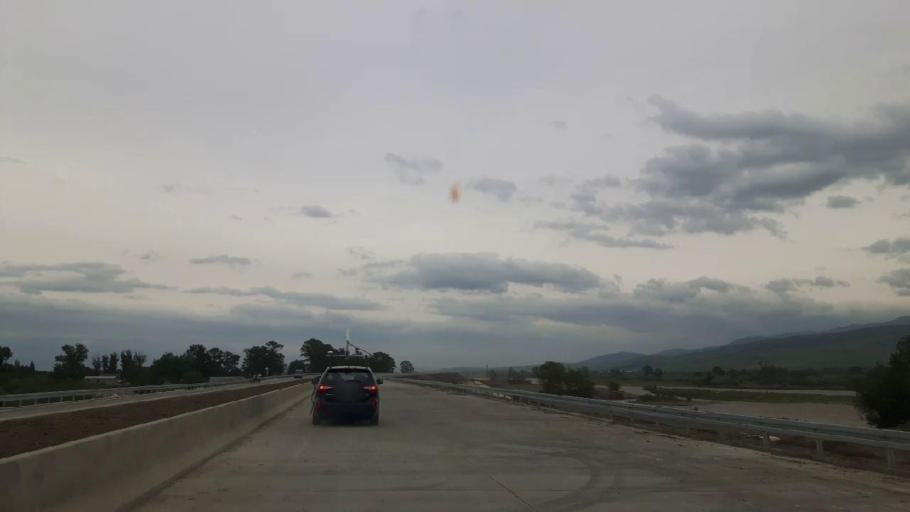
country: GE
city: Agara
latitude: 42.0156
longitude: 43.7315
